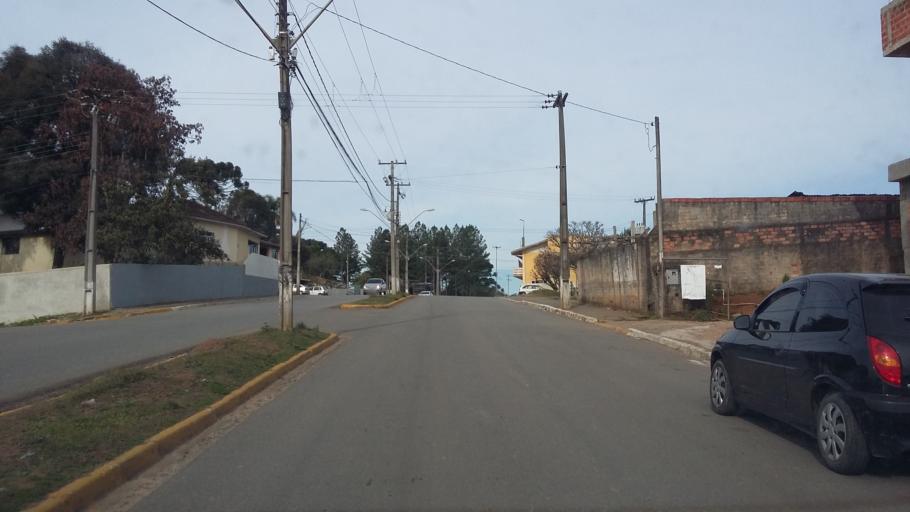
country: BR
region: Parana
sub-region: Lapa
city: Lapa
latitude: -25.8781
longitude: -49.4936
